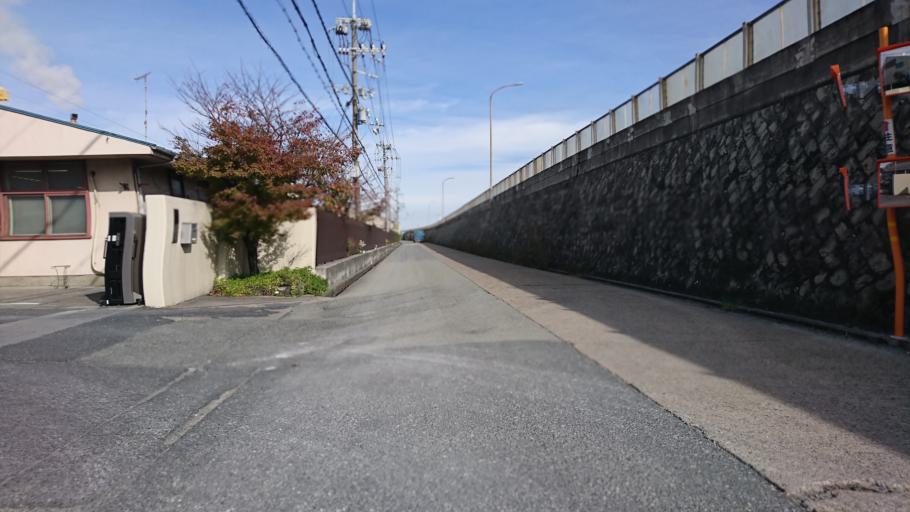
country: JP
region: Hyogo
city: Kakogawacho-honmachi
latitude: 34.7429
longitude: 134.8067
